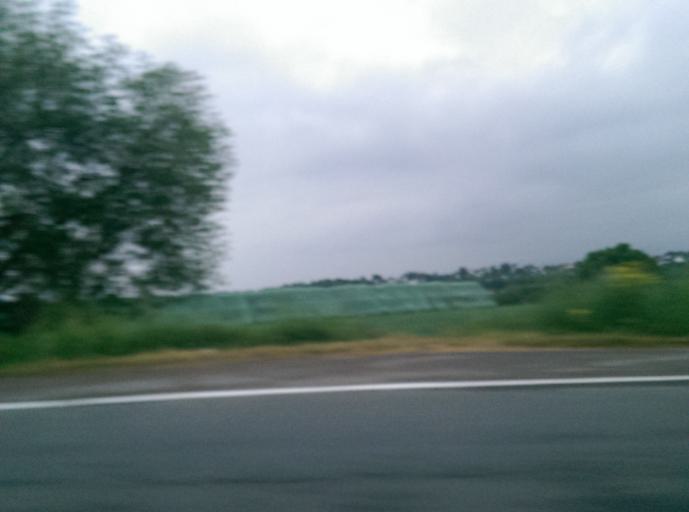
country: DE
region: Rheinland-Pfalz
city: Melsbach
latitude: 50.4688
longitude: 7.4776
